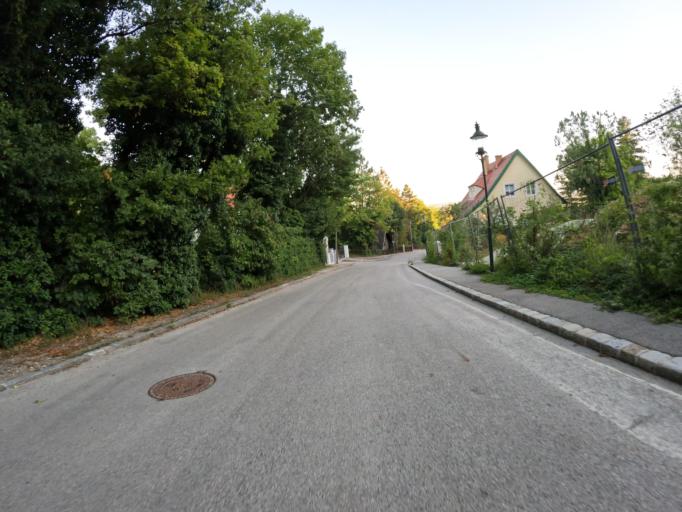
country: AT
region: Lower Austria
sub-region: Politischer Bezirk Baden
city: Baden
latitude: 48.0164
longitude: 16.2245
